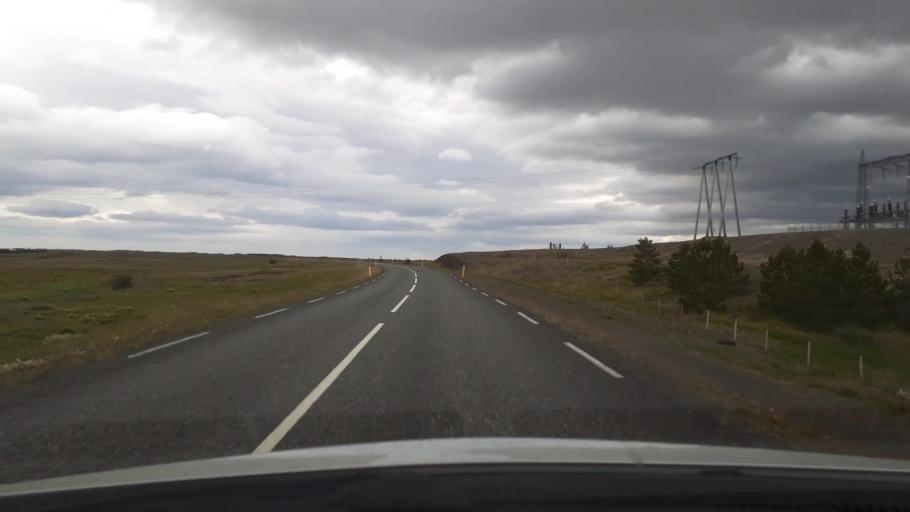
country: IS
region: West
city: Borgarnes
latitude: 64.5539
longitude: -21.7166
